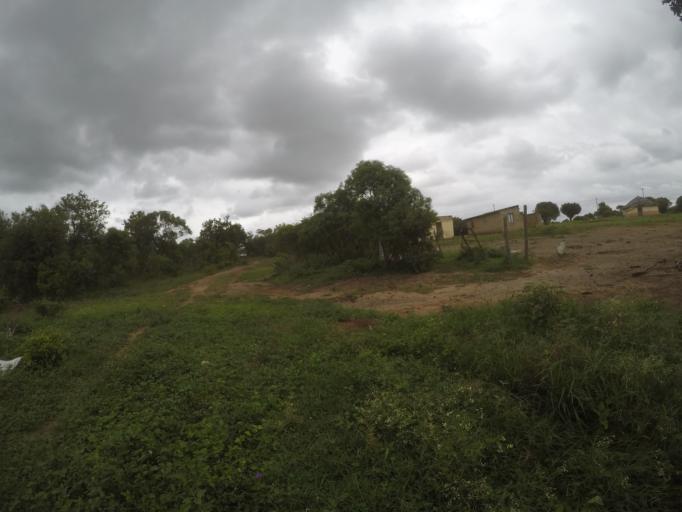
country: ZA
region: KwaZulu-Natal
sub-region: uThungulu District Municipality
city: Empangeni
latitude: -28.5921
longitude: 31.8466
